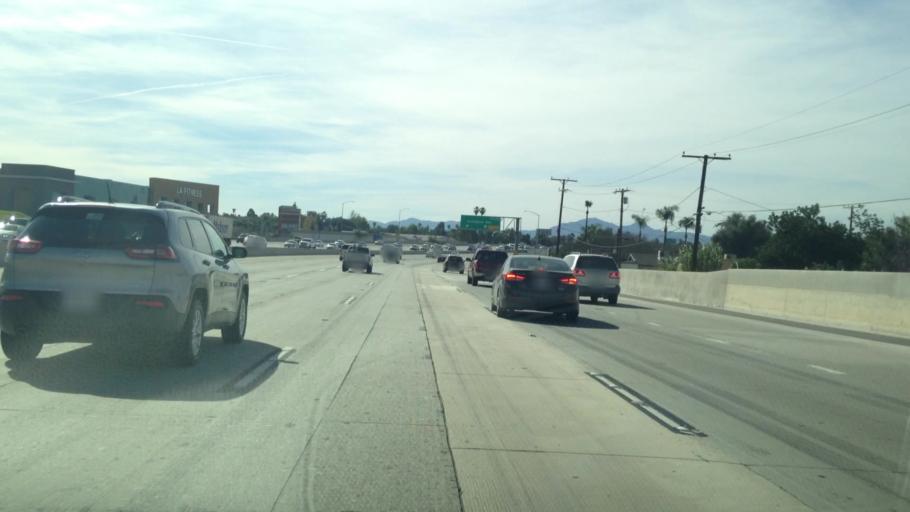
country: US
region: California
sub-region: Riverside County
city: Riverside
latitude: 33.9505
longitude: -117.3857
